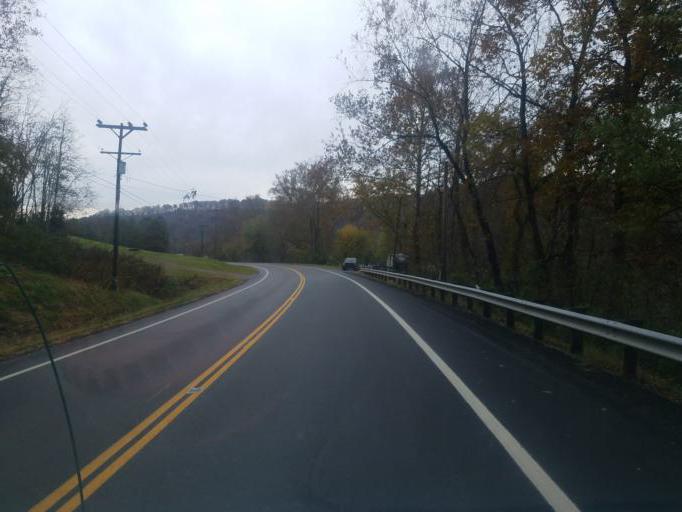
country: US
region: Ohio
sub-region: Washington County
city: Devola
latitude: 39.5350
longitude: -81.5446
